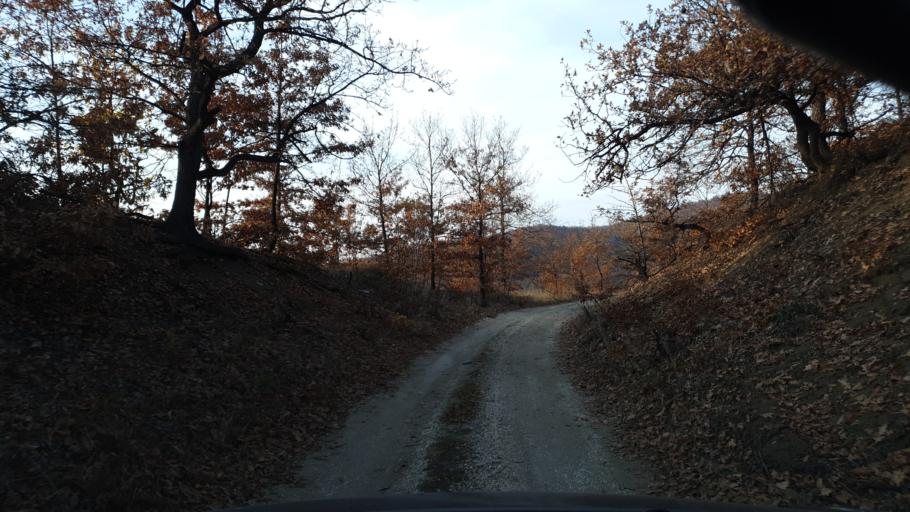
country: RS
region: Central Serbia
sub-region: Borski Okrug
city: Bor
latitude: 44.0687
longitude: 22.0747
